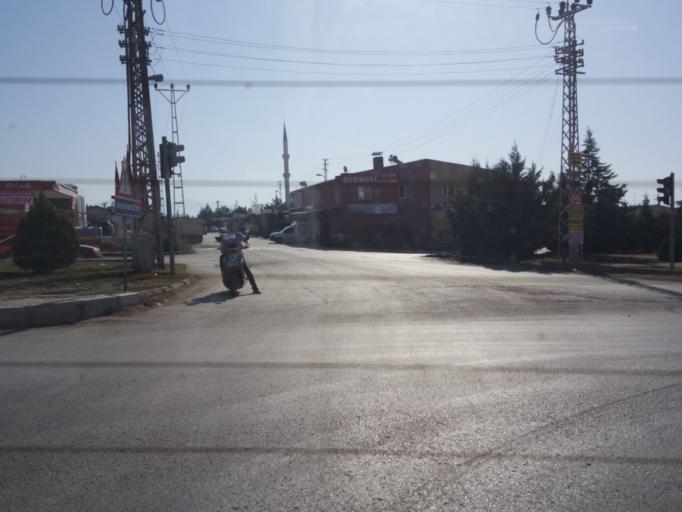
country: TR
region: Amasya
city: Merzifon
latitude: 40.8621
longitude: 35.4636
